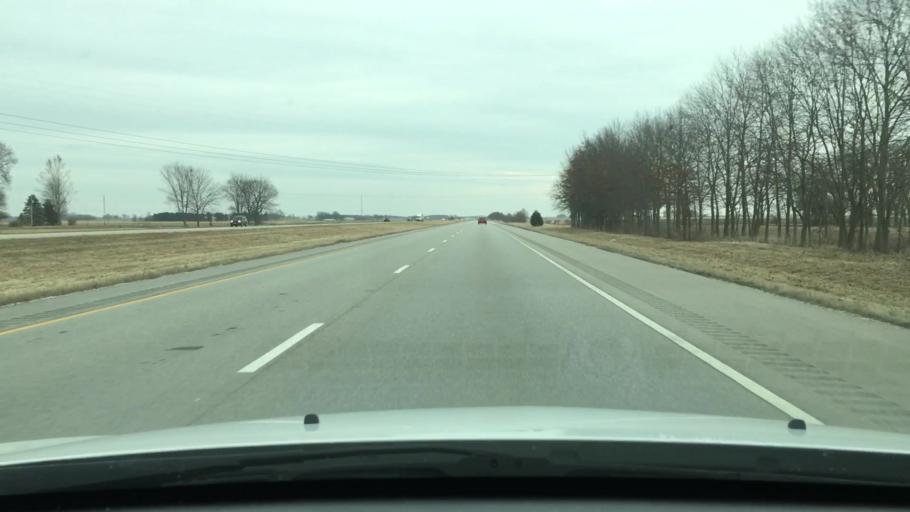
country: US
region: Illinois
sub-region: Sangamon County
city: New Berlin
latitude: 39.7368
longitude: -90.0162
